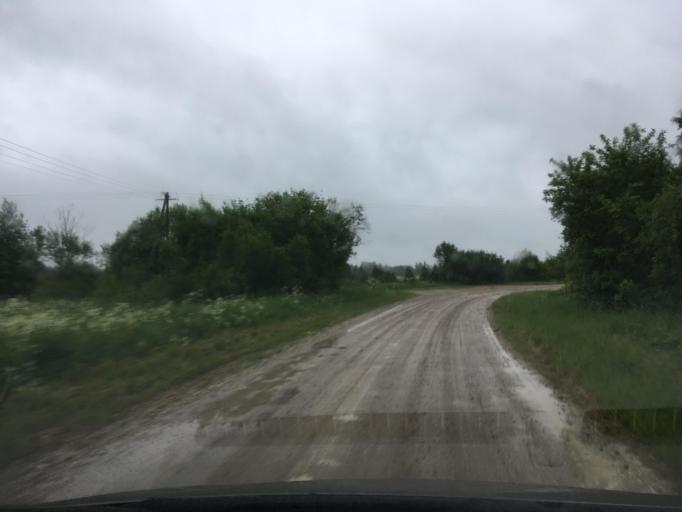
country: EE
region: Laeaene
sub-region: Lihula vald
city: Lihula
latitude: 58.5936
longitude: 23.8463
